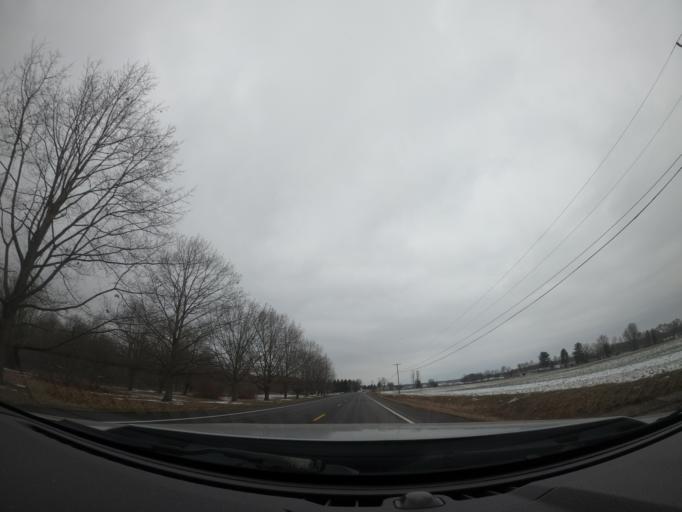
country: US
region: New York
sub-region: Cayuga County
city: Moravia
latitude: 42.6329
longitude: -76.4943
